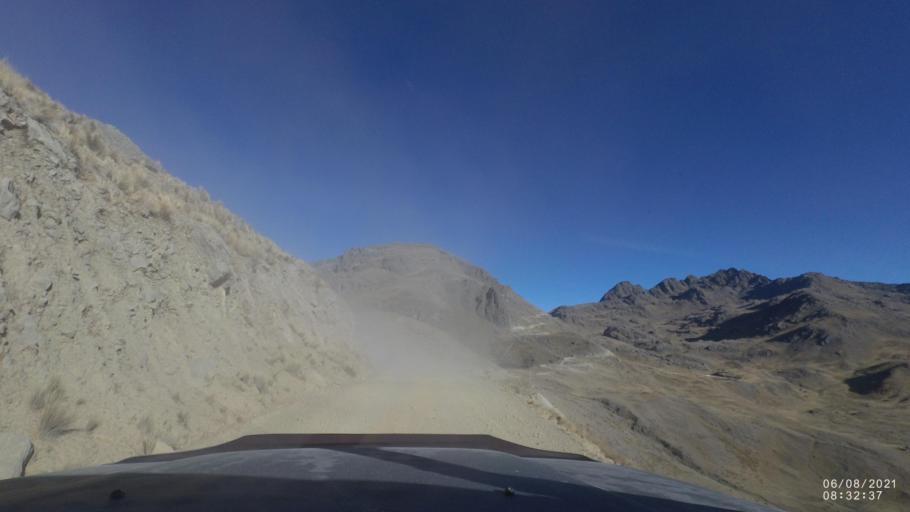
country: BO
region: Cochabamba
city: Sipe Sipe
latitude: -17.1816
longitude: -66.3735
